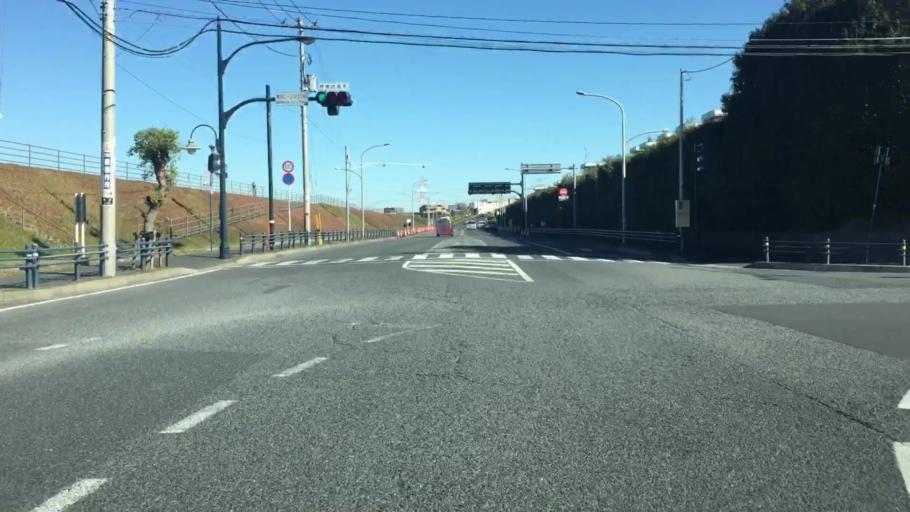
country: JP
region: Tokyo
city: Urayasu
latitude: 35.6408
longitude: 139.8799
